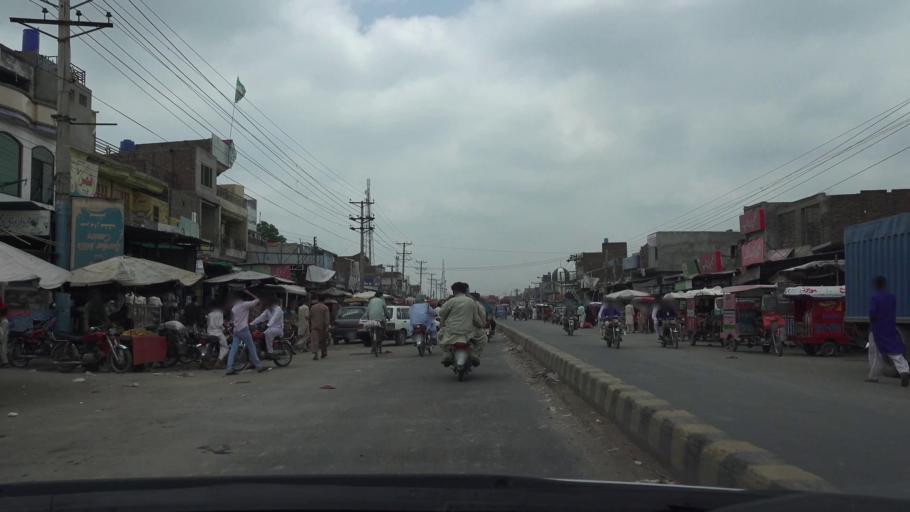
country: PK
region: Punjab
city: Faisalabad
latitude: 31.3886
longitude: 73.1965
